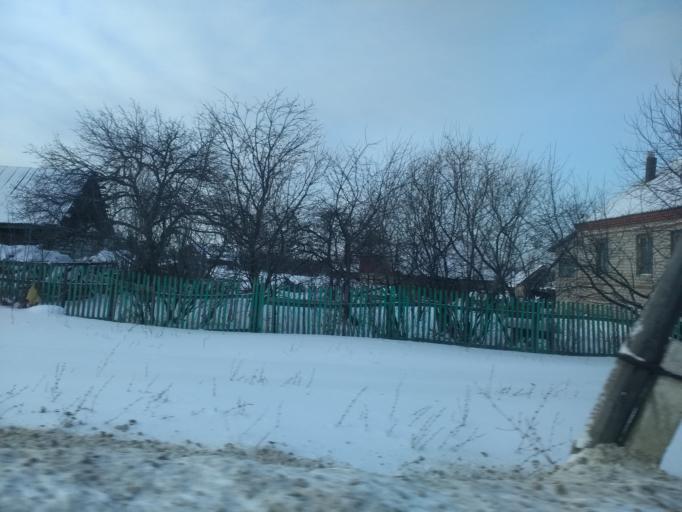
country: RU
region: Bashkortostan
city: Iglino
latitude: 54.7745
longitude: 56.5367
